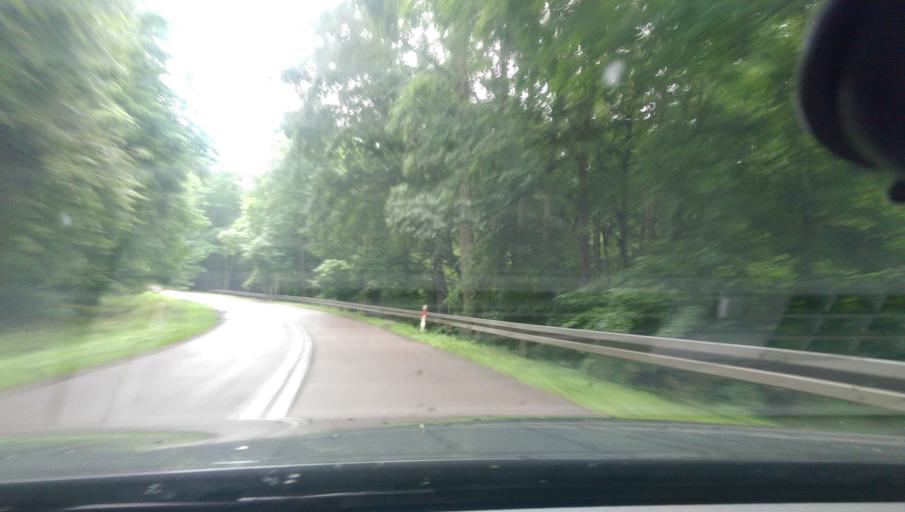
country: PL
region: Warmian-Masurian Voivodeship
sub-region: Powiat mragowski
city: Piecki
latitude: 53.7080
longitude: 21.4391
